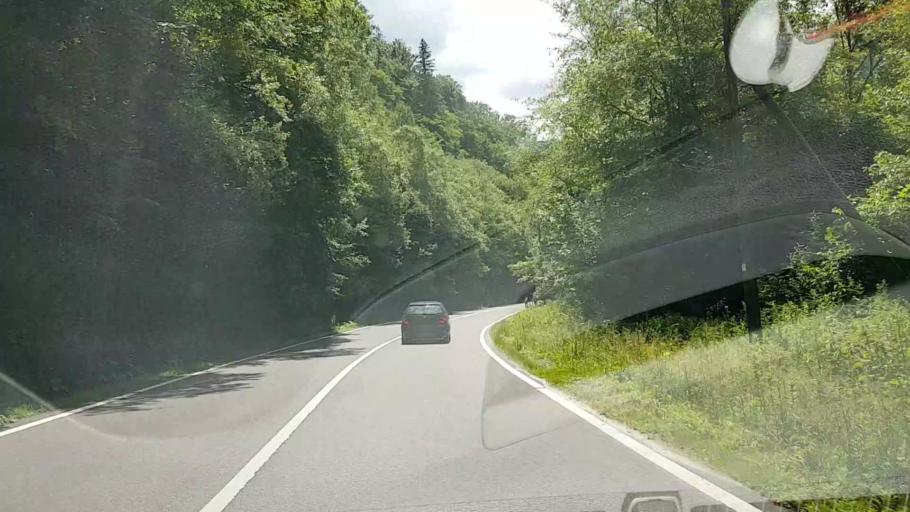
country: RO
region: Suceava
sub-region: Comuna Brosteni
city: Brosteni
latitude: 47.2804
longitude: 25.6502
